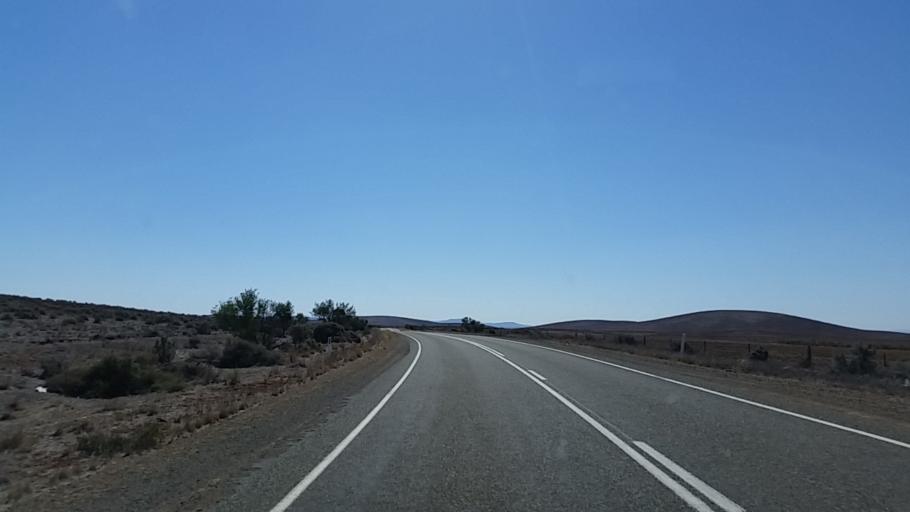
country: AU
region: South Australia
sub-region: Flinders Ranges
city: Quorn
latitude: -32.1603
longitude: 138.5312
